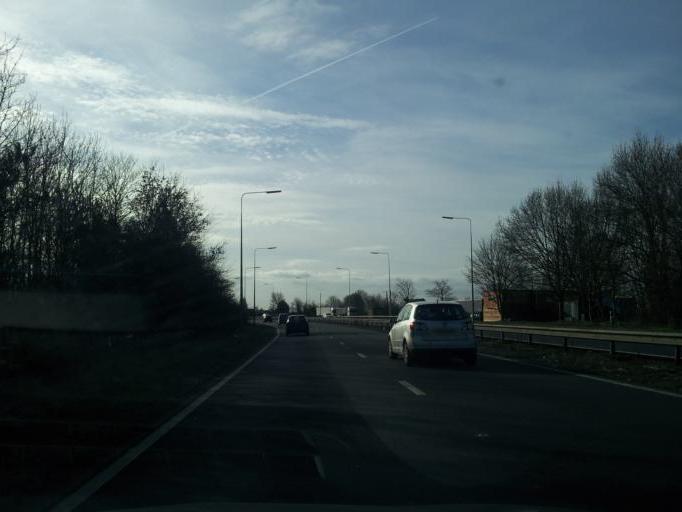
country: GB
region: England
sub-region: Central Bedfordshire
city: Sandy
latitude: 52.1110
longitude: -0.2830
